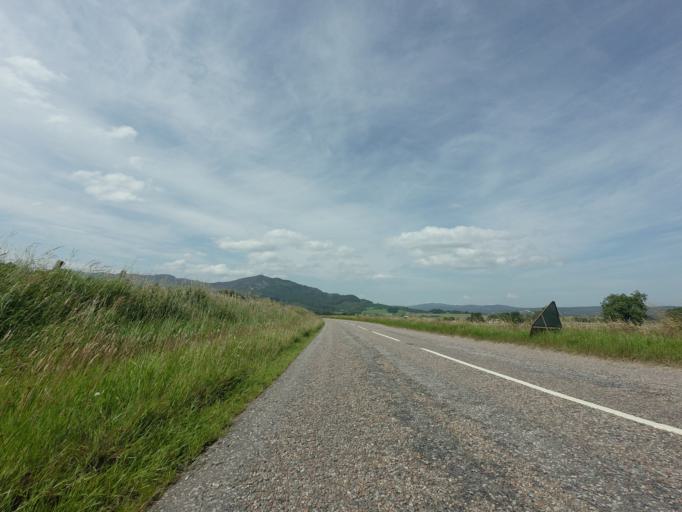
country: GB
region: Scotland
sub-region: Highland
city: Tain
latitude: 57.8390
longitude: -4.1882
